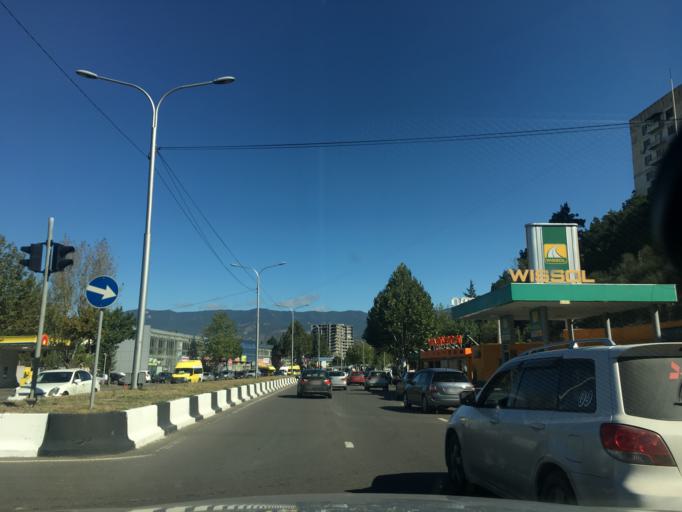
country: GE
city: Zahesi
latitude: 41.7787
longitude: 44.7960
